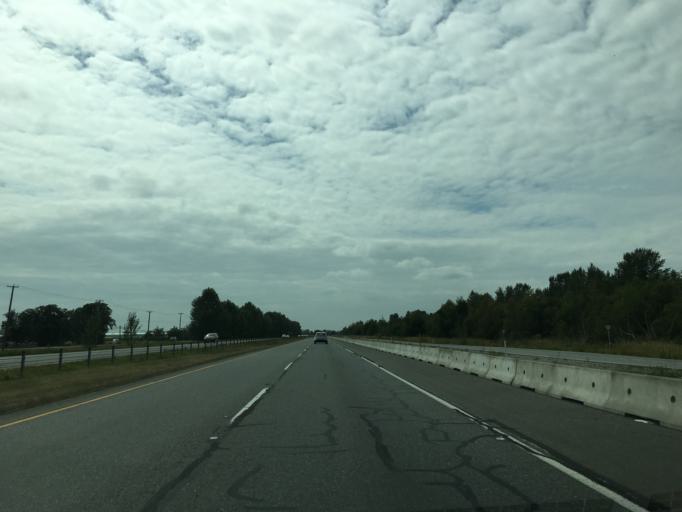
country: CA
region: British Columbia
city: Delta
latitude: 49.0905
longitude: -122.9858
